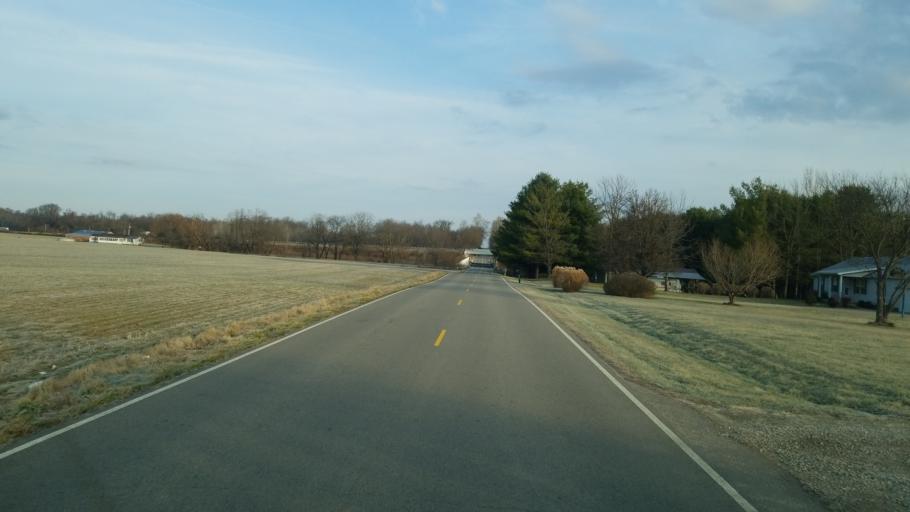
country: US
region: Ohio
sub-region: Ross County
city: Chillicothe
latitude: 39.2613
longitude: -82.8703
